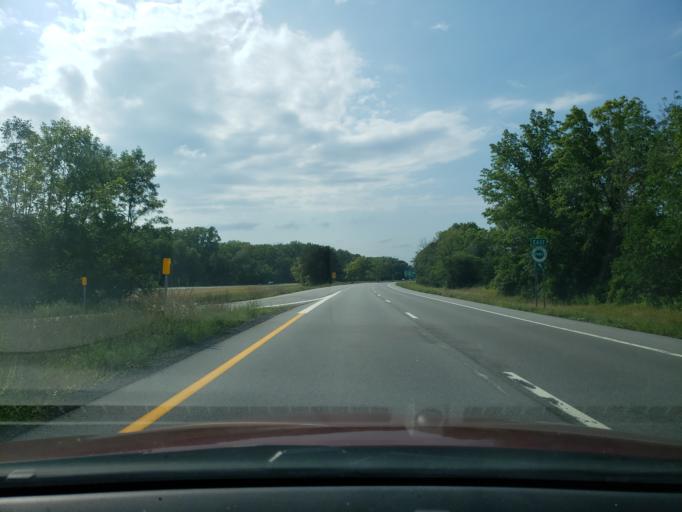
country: US
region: New York
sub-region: Monroe County
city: Irondequoit
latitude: 43.2570
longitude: -77.6348
